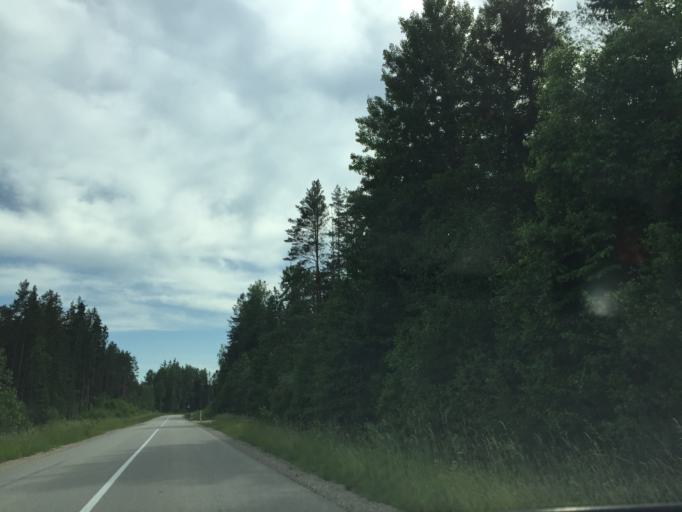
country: LV
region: Tukuma Rajons
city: Tukums
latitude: 57.0259
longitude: 23.2501
